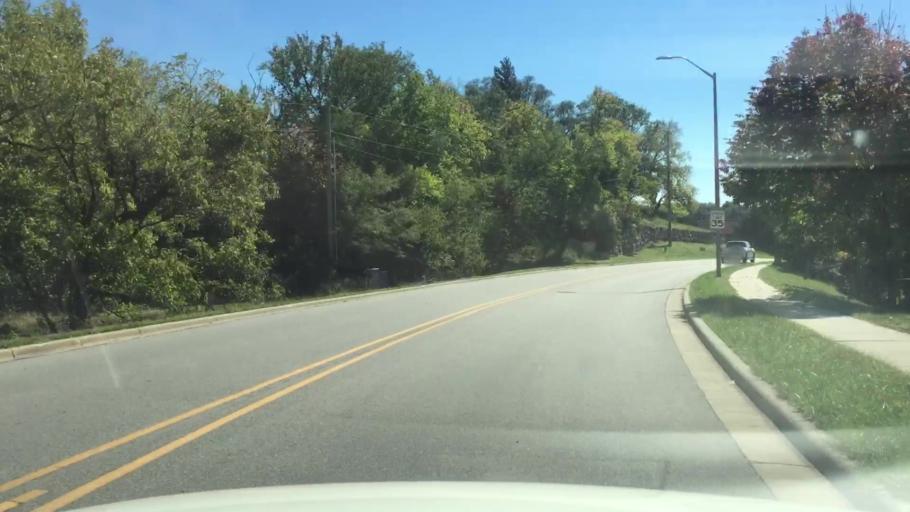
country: US
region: Kansas
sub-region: Johnson County
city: Shawnee
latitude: 39.0356
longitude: -94.7500
